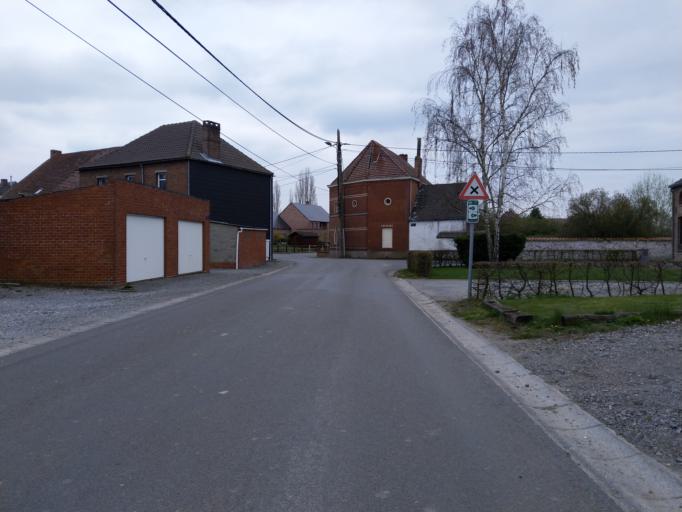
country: BE
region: Wallonia
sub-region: Province du Hainaut
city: Lens
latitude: 50.5286
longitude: 3.8518
